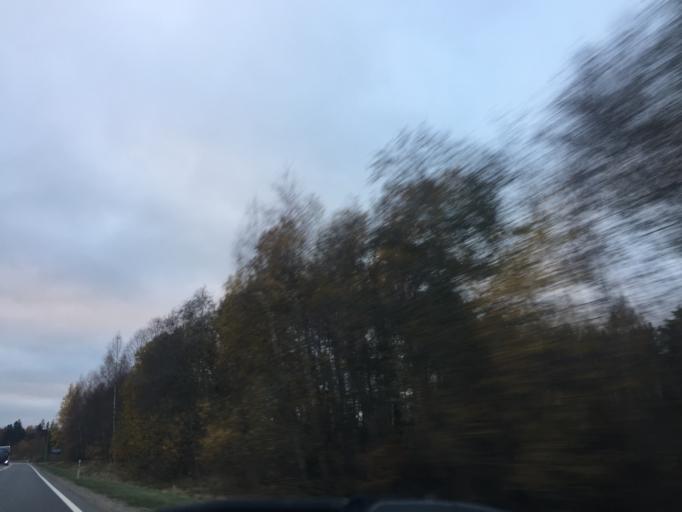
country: LV
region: Aizpute
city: Aizpute
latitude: 56.5974
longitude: 21.7310
